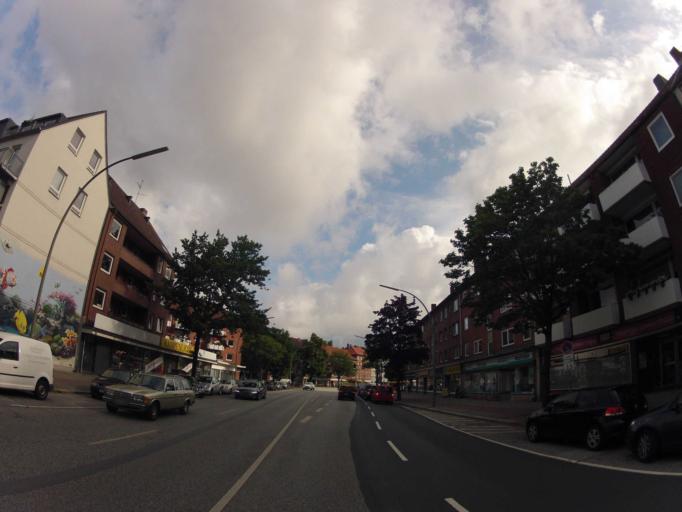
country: DE
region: Hamburg
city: Hamburg
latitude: 53.5796
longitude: 10.0191
